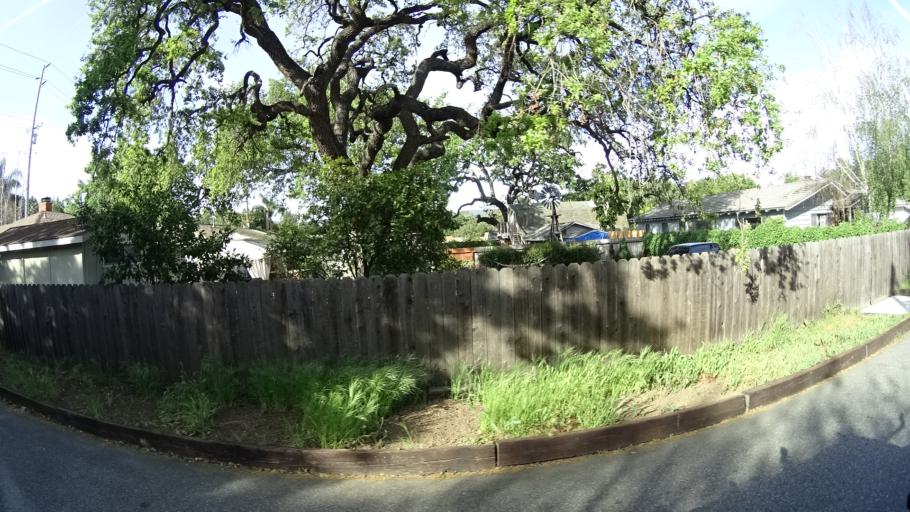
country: US
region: California
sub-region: Ventura County
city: Thousand Oaks
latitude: 34.1867
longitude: -118.8661
